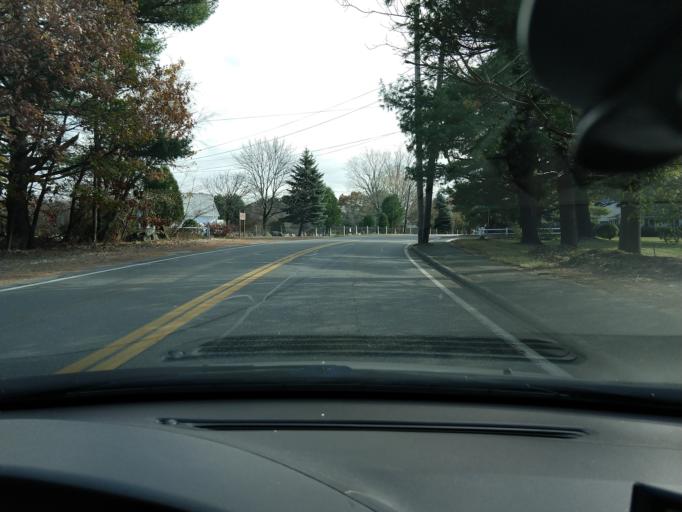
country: US
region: Massachusetts
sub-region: Middlesex County
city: Burlington
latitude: 42.5058
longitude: -71.2159
